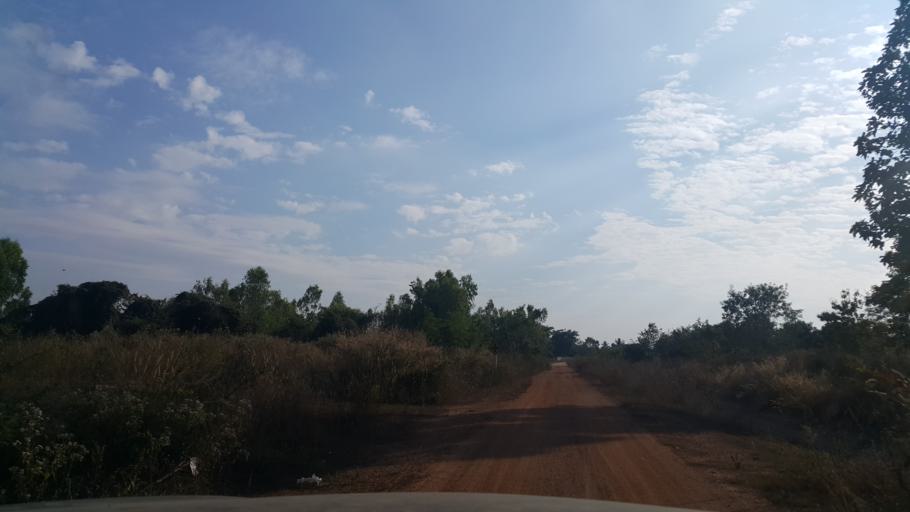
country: TH
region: Lampang
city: Ko Kha
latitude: 18.2346
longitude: 99.3572
